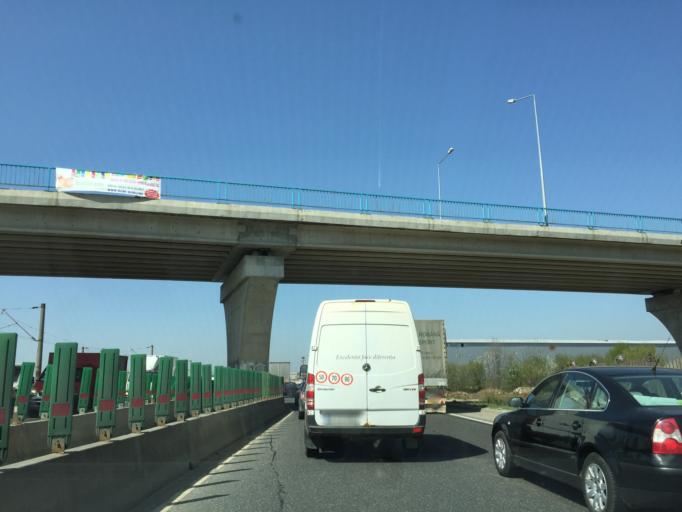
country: RO
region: Ilfov
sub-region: Comuna Tunari
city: Tunari
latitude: 44.5356
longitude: 26.1430
